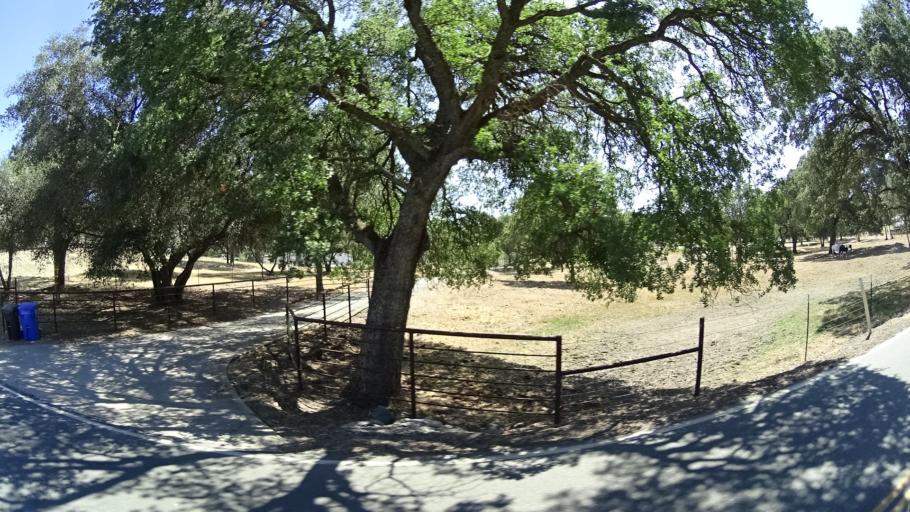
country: US
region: California
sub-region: Calaveras County
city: Rancho Calaveras
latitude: 38.1660
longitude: -120.9088
